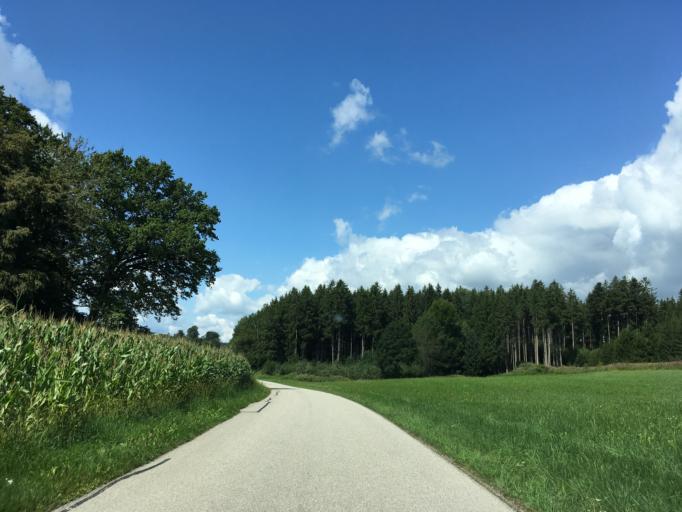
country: DE
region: Bavaria
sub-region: Upper Bavaria
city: Pittenhart
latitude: 47.9731
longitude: 12.3684
